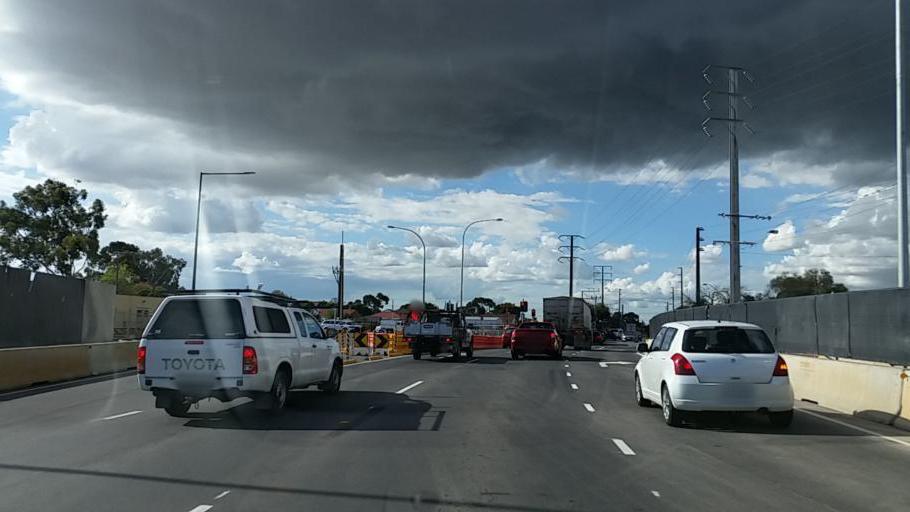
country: AU
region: South Australia
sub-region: Charles Sturt
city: Allenby Gardens
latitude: -34.8891
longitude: 138.5695
